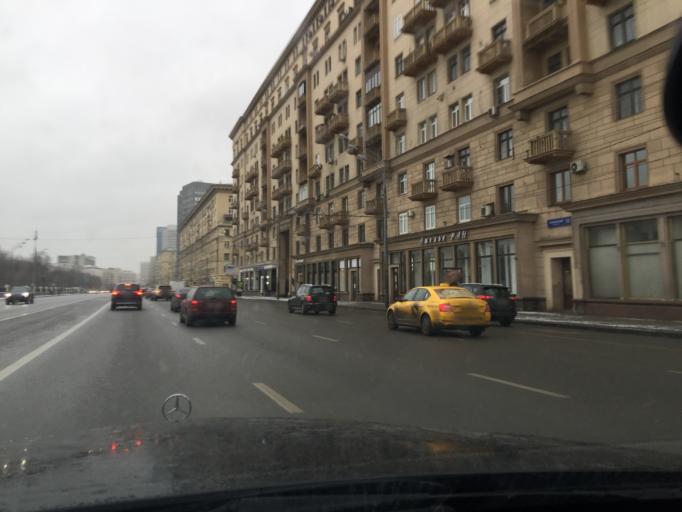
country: RU
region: Moscow
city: Novyye Cheremushki
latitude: 55.7217
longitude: 37.6011
